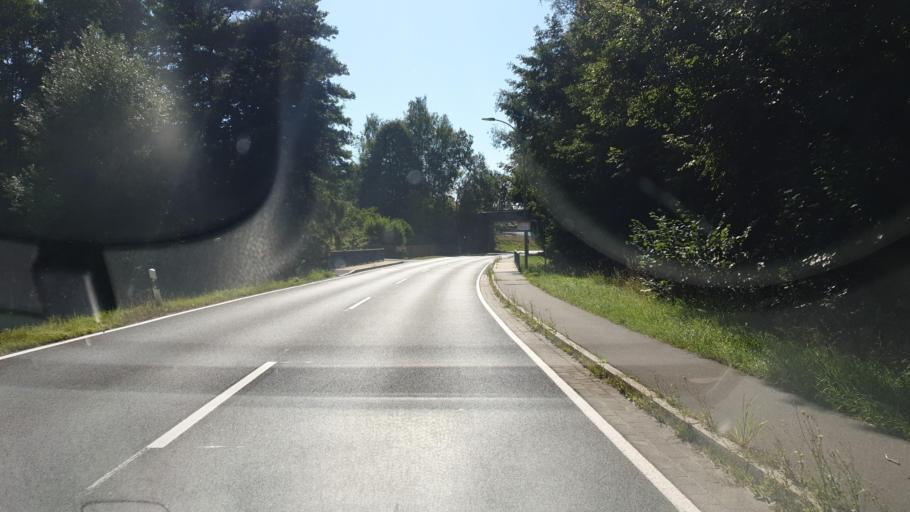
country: DE
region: Saxony
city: Lengenfeld
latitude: 50.5787
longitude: 12.3702
